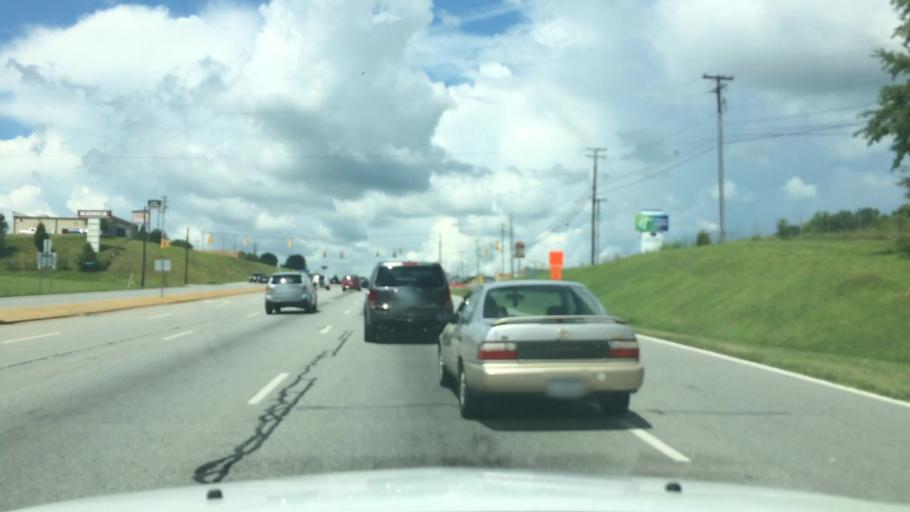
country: US
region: North Carolina
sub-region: Wilkes County
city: Cricket
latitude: 36.1505
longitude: -81.1880
